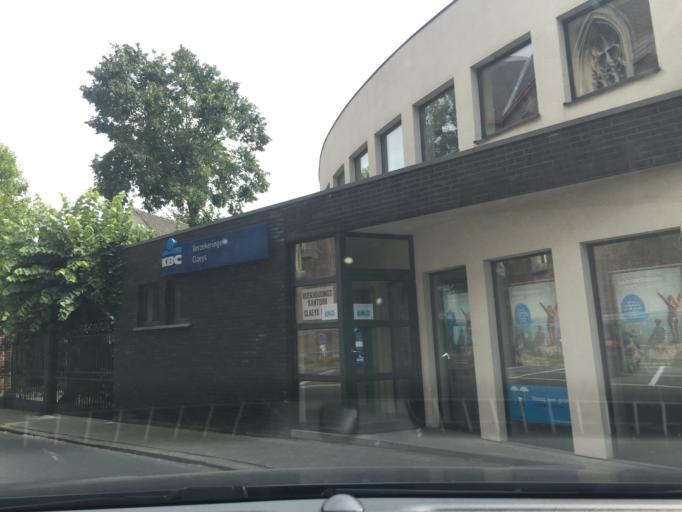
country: BE
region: Flanders
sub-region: Provincie West-Vlaanderen
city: Izegem
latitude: 50.9169
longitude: 3.2142
